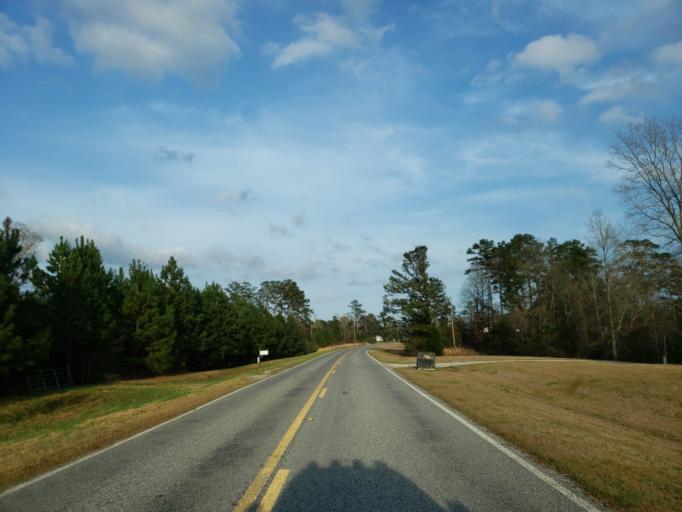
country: US
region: Mississippi
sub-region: Clarke County
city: Stonewall
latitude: 32.1732
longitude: -88.6850
